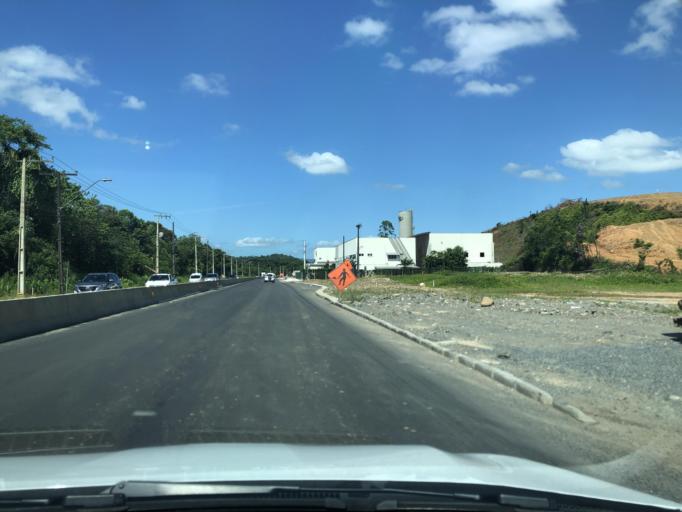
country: BR
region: Santa Catarina
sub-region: Joinville
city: Joinville
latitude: -26.2523
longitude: -48.8685
